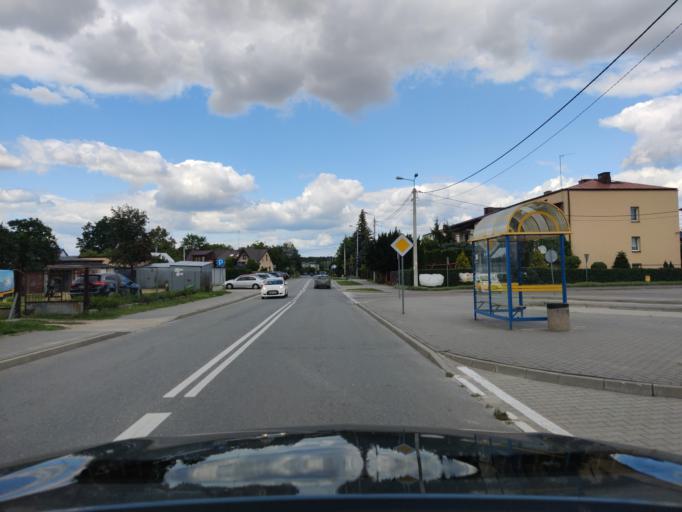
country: PL
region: Masovian Voivodeship
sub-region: Powiat wegrowski
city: Wegrow
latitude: 52.3994
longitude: 22.0200
